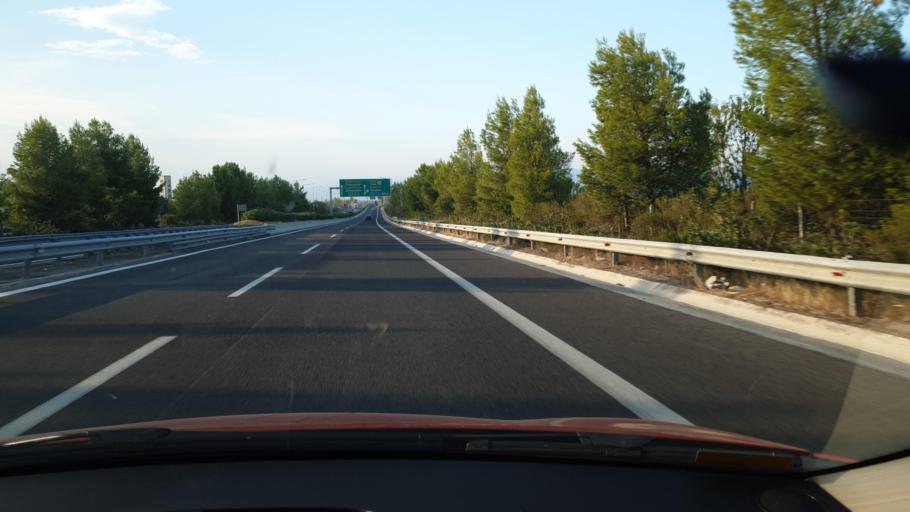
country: GR
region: Thessaly
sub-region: Nomos Magnisias
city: Velestino
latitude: 39.3777
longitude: 22.7692
